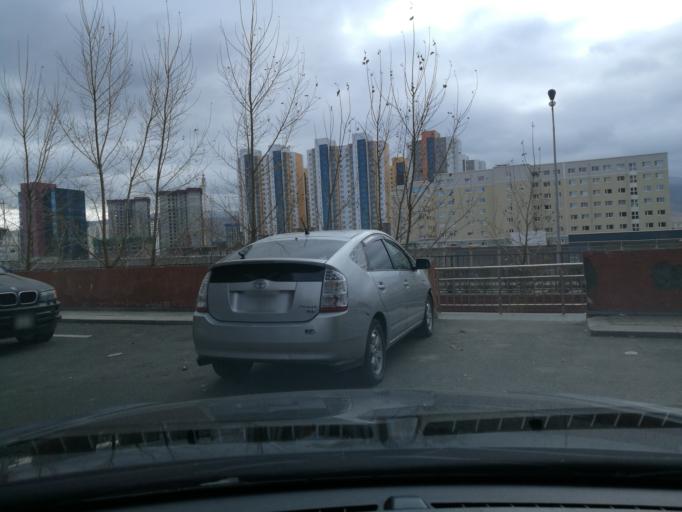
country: MN
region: Ulaanbaatar
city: Ulaanbaatar
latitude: 47.9001
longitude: 106.9203
